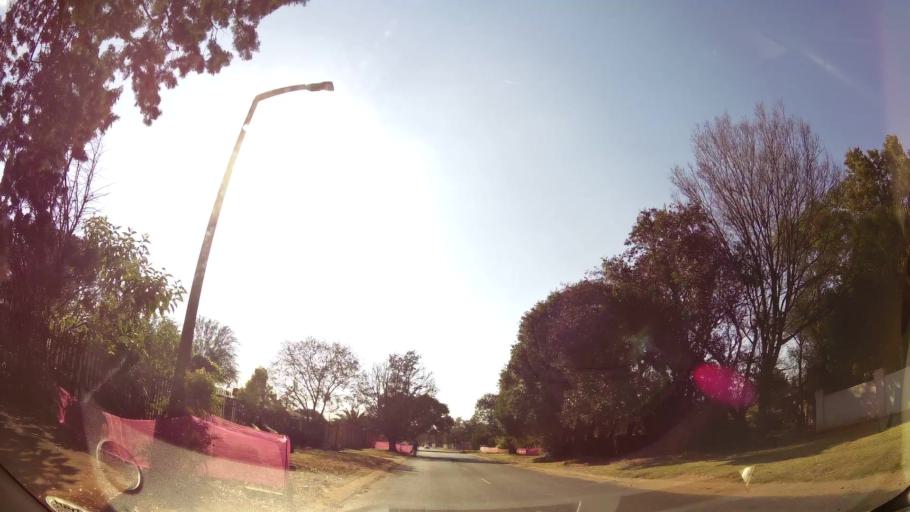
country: ZA
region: Gauteng
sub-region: Ekurhuleni Metropolitan Municipality
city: Benoni
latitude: -26.1480
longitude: 28.3129
